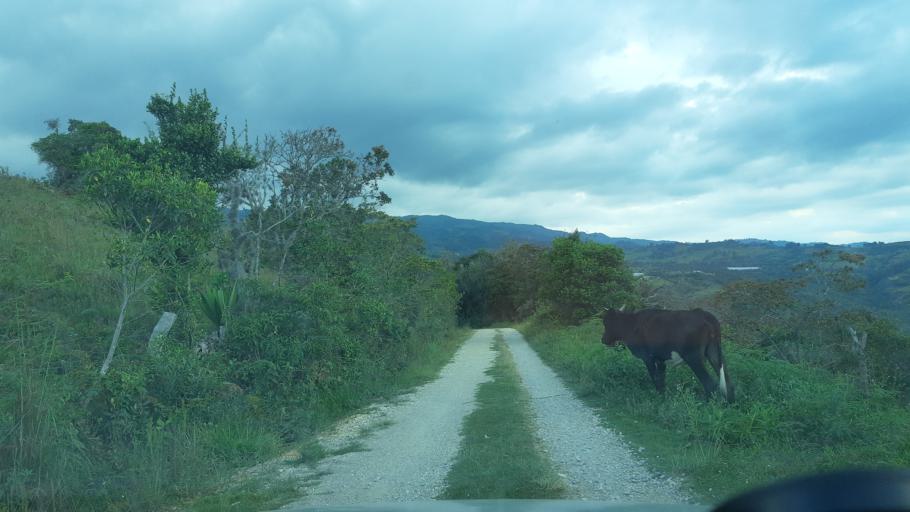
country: CO
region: Boyaca
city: Santa Sofia
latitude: 5.7492
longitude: -73.5753
